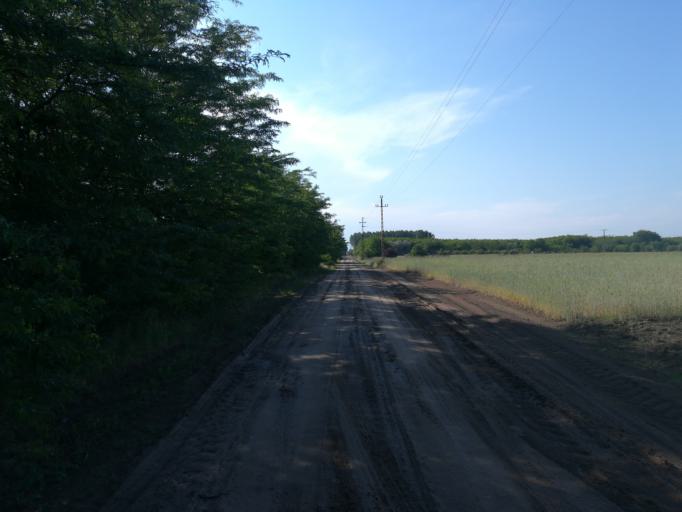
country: HU
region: Bacs-Kiskun
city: Tiszakecske
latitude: 46.9429
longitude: 20.0873
